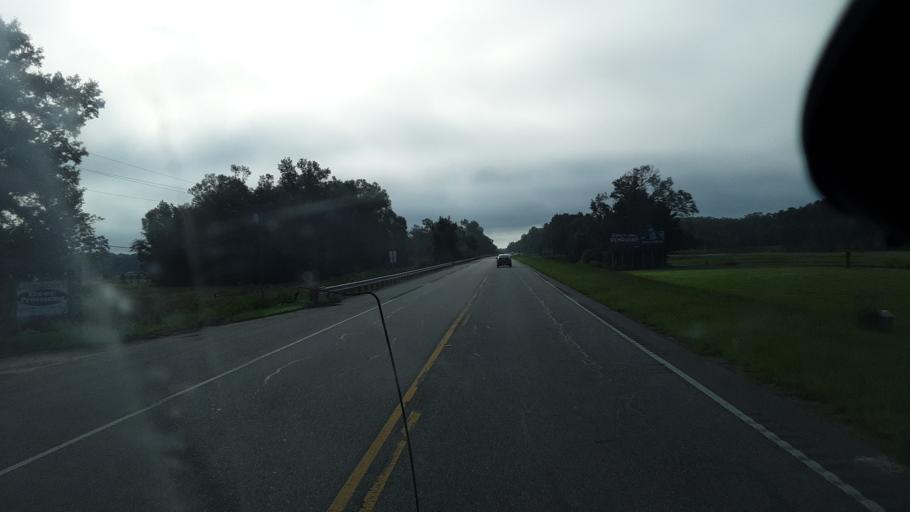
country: US
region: South Carolina
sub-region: Horry County
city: Red Hill
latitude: 33.8459
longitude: -79.2843
